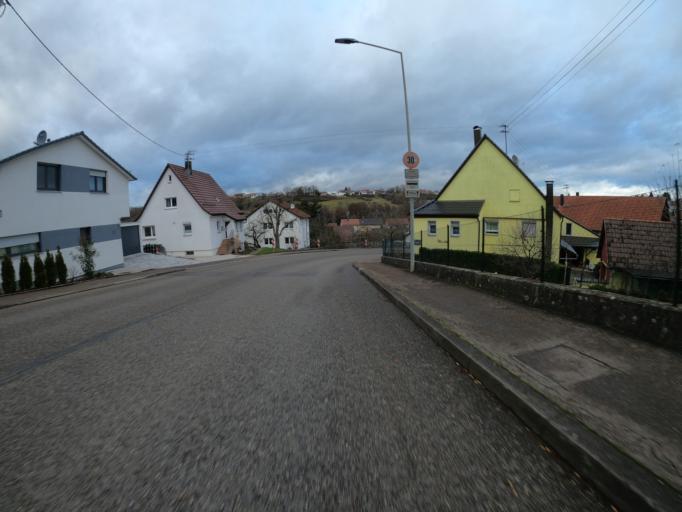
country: DE
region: Baden-Wuerttemberg
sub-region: Regierungsbezirk Stuttgart
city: Waldstetten
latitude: 48.7827
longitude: 9.8390
